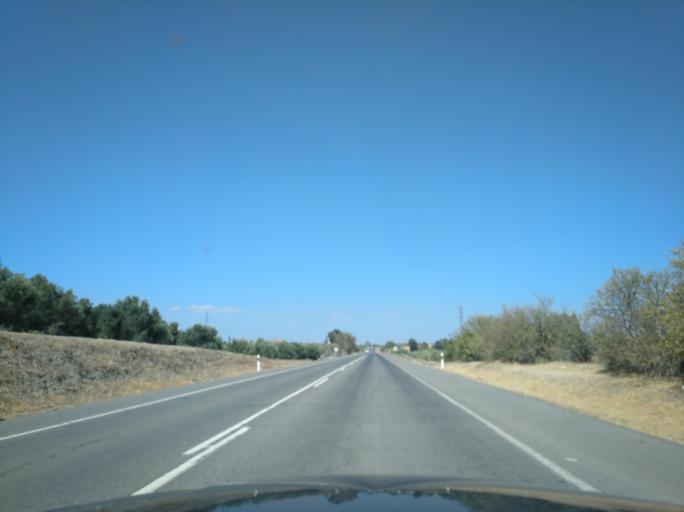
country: ES
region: Andalusia
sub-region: Provincia de Huelva
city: Gibraleon
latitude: 37.3447
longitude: -7.0206
